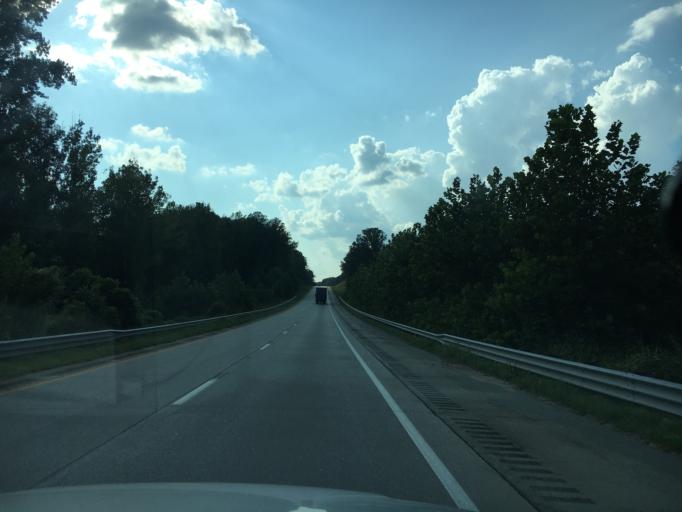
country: US
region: South Carolina
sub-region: Laurens County
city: Clinton
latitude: 34.5140
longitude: -81.8725
